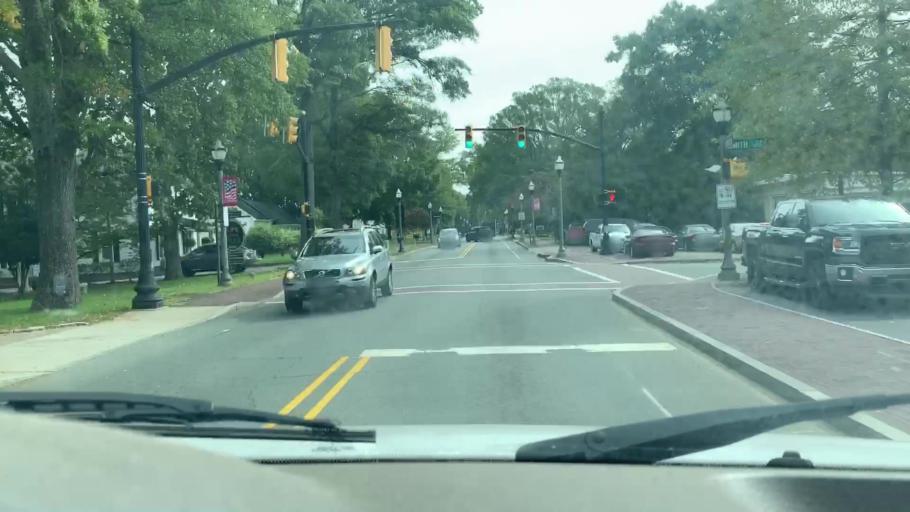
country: US
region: North Carolina
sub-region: Mecklenburg County
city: Cornelius
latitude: 35.4838
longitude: -80.8675
